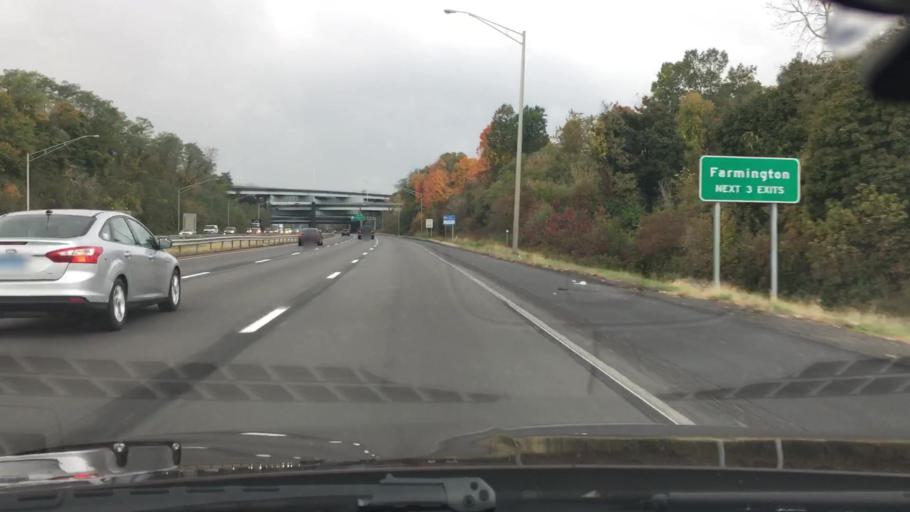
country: US
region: Connecticut
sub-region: Hartford County
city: West Hartford
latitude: 41.7263
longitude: -72.7661
